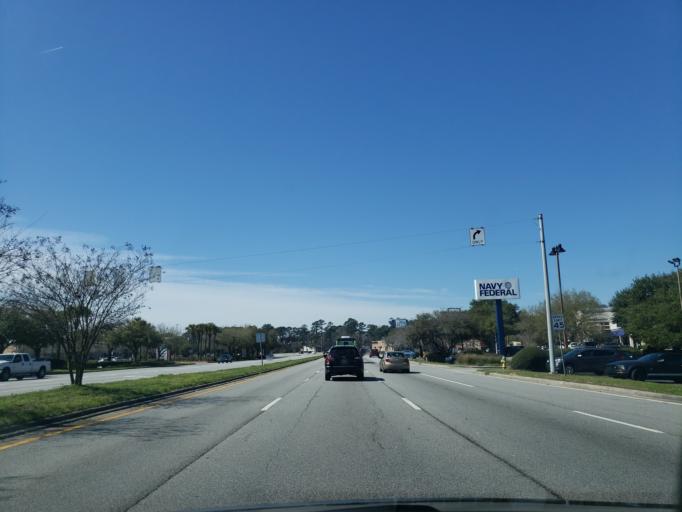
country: US
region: Georgia
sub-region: Chatham County
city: Montgomery
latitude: 32.0046
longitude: -81.1219
